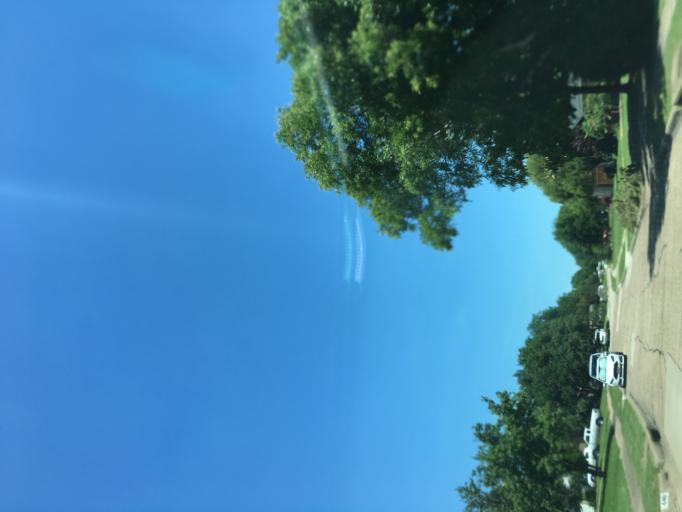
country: US
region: Texas
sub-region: Dallas County
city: Richardson
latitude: 32.9703
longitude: -96.7342
